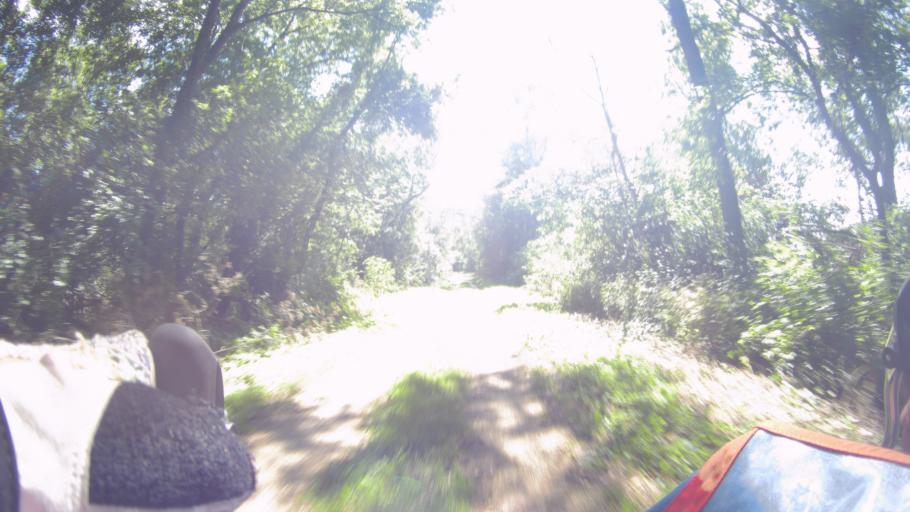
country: US
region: Wisconsin
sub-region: Dane County
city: Fitchburg
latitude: 42.9338
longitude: -89.4996
